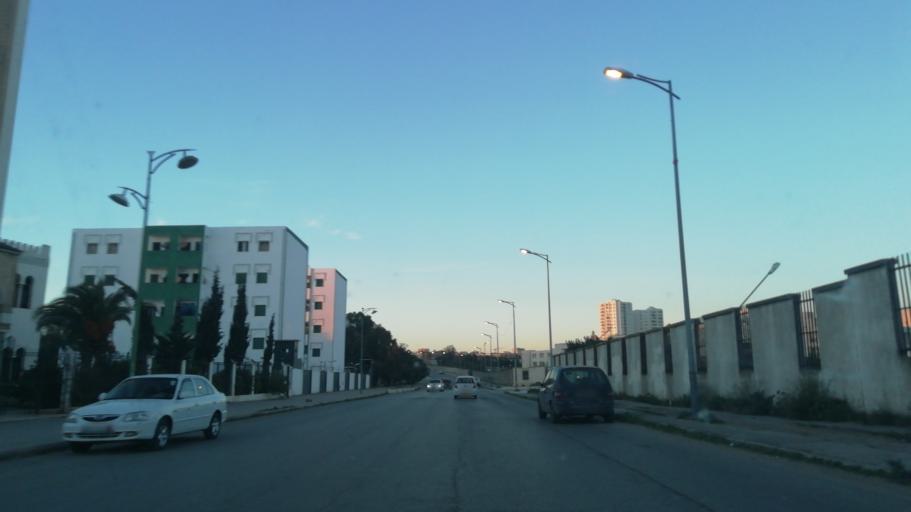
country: DZ
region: Oran
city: Bir el Djir
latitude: 35.7046
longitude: -0.5853
